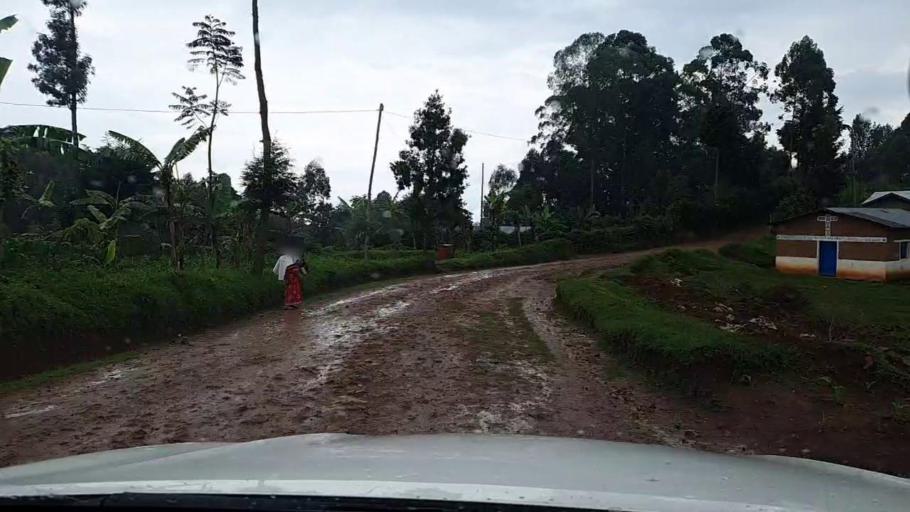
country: RW
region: Western Province
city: Cyangugu
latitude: -2.5454
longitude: 28.9783
